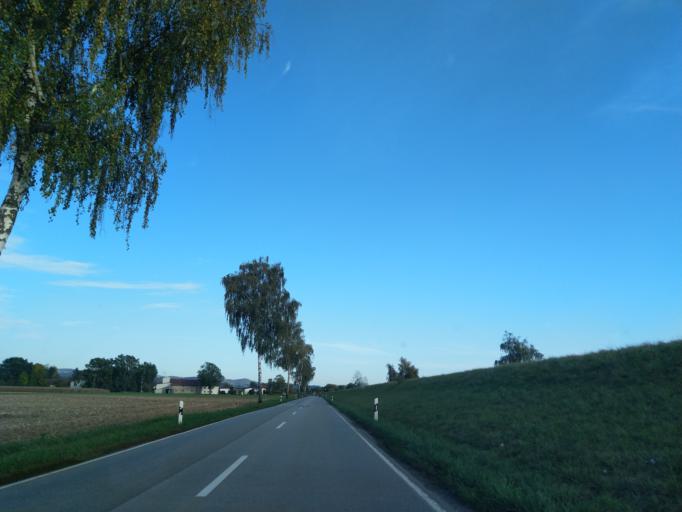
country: DE
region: Bavaria
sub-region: Lower Bavaria
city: Offenberg
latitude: 48.8439
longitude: 12.8669
